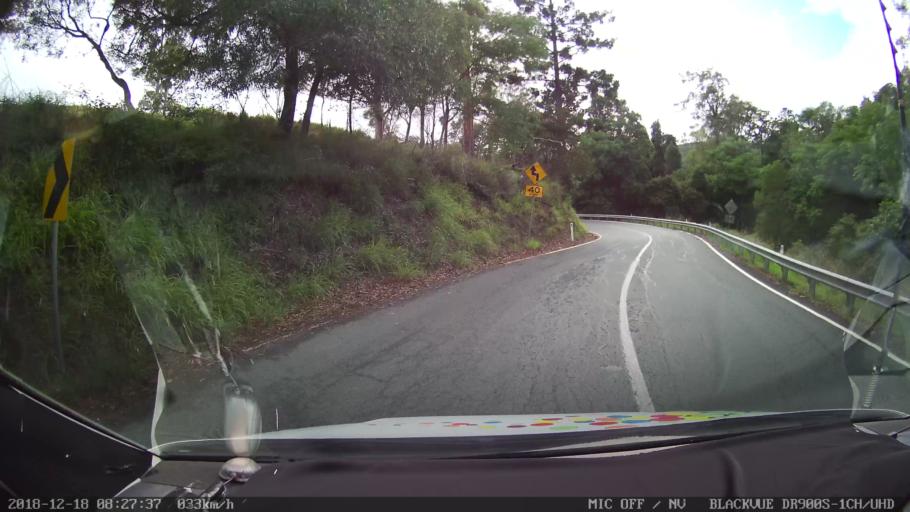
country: AU
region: New South Wales
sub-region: Kyogle
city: Kyogle
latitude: -28.3254
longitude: 152.7502
